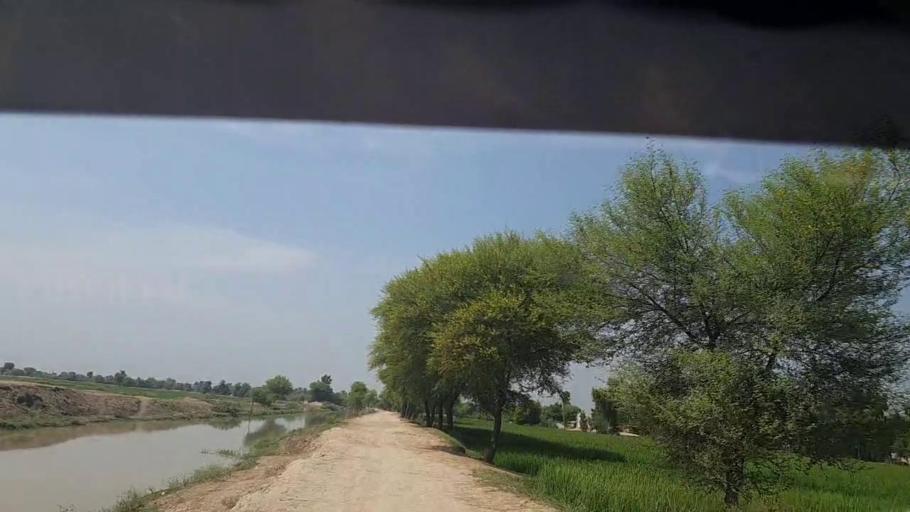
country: PK
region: Sindh
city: Thul
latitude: 28.2007
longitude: 68.7003
